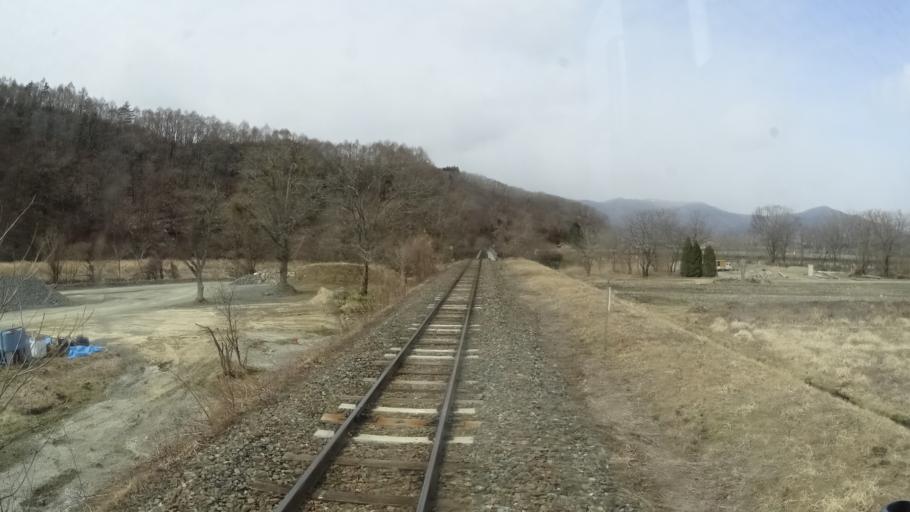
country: JP
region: Iwate
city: Tono
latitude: 39.3258
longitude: 141.5533
